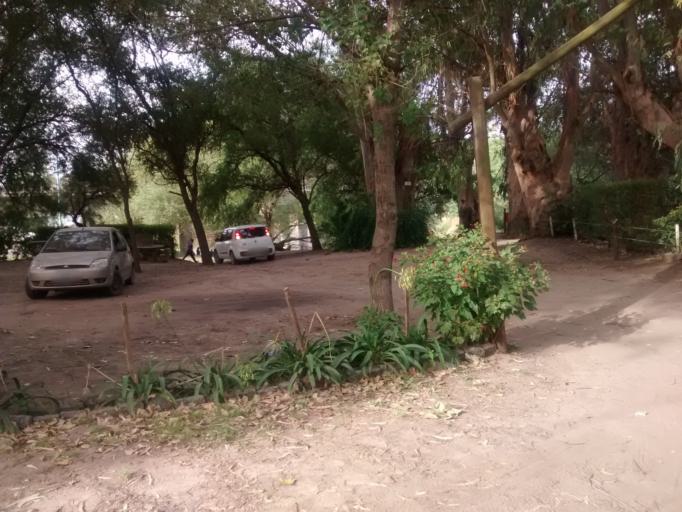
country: AR
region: Buenos Aires
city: Necochea
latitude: -38.4612
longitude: -58.7619
